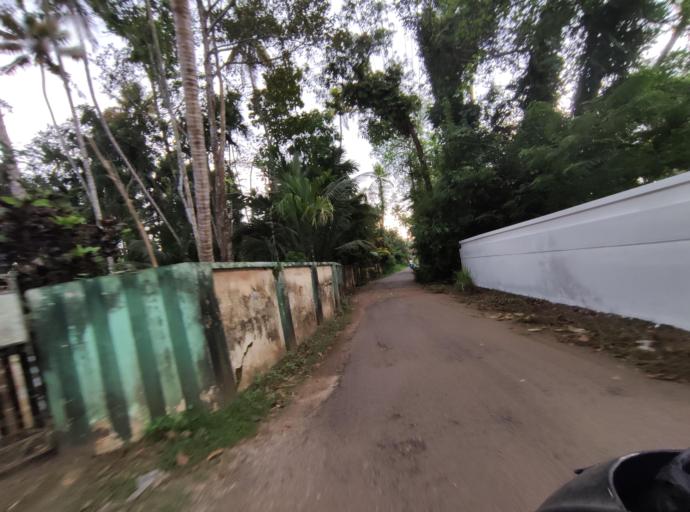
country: IN
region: Kerala
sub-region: Alappuzha
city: Shertallai
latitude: 9.6704
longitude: 76.3465
